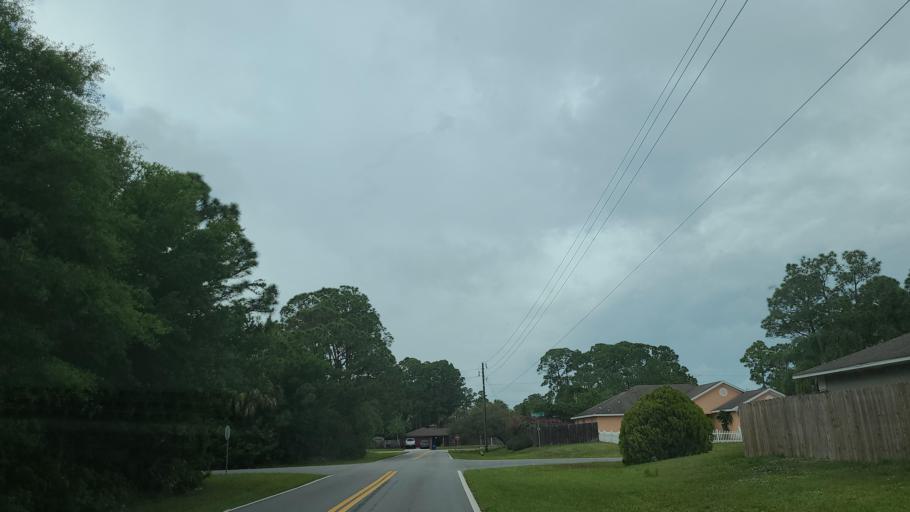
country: US
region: Florida
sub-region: Brevard County
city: Grant-Valkaria
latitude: 27.9421
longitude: -80.6338
